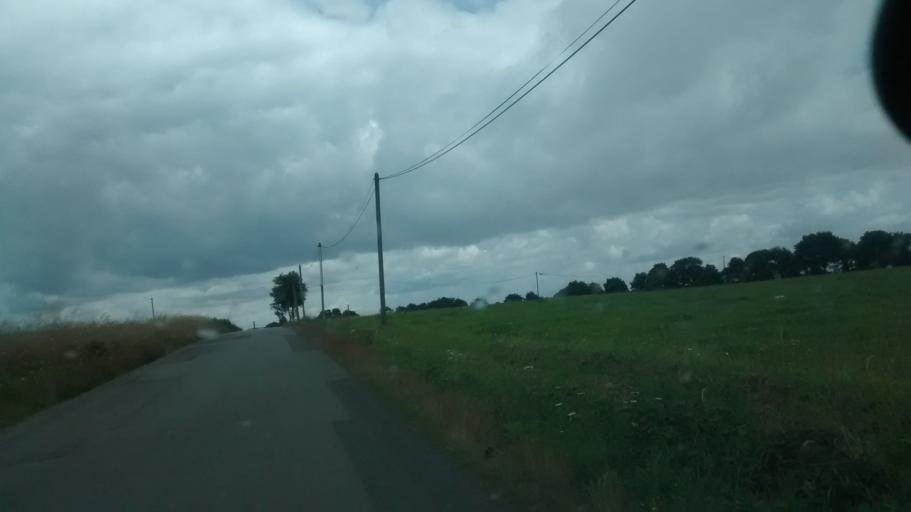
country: FR
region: Brittany
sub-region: Departement d'Ille-et-Vilaine
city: Grand-Fougeray
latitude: 47.7703
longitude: -1.7462
